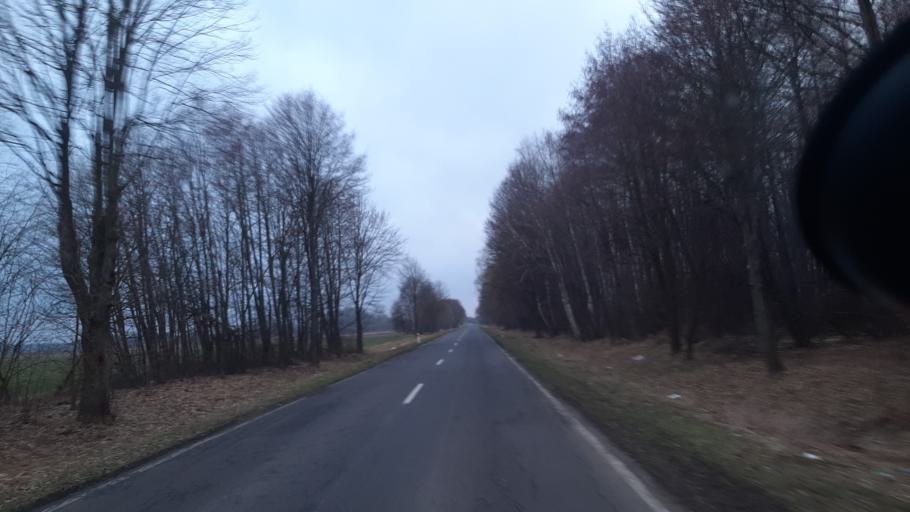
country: PL
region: Lublin Voivodeship
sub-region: Powiat parczewski
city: Sosnowica
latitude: 51.6175
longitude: 23.1040
